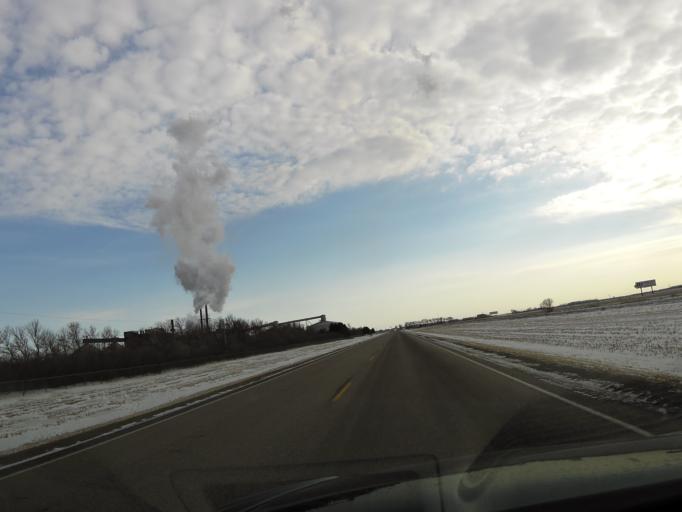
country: US
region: Minnesota
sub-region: Kittson County
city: Hallock
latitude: 48.5974
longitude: -97.1788
